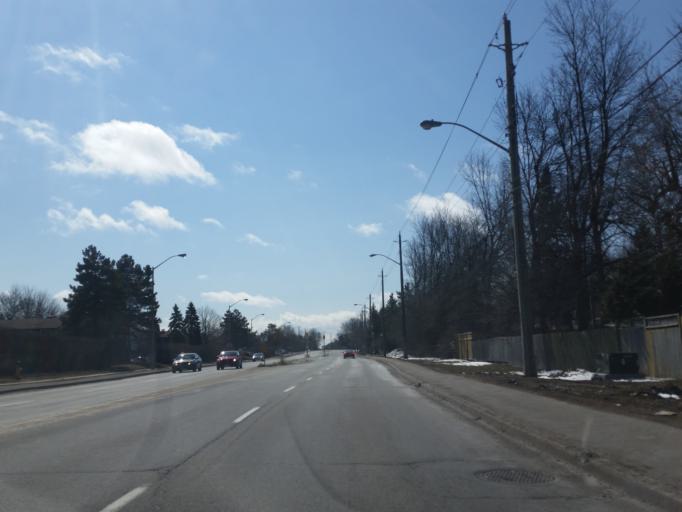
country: CA
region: Ontario
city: Bells Corners
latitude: 45.3183
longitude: -75.8310
